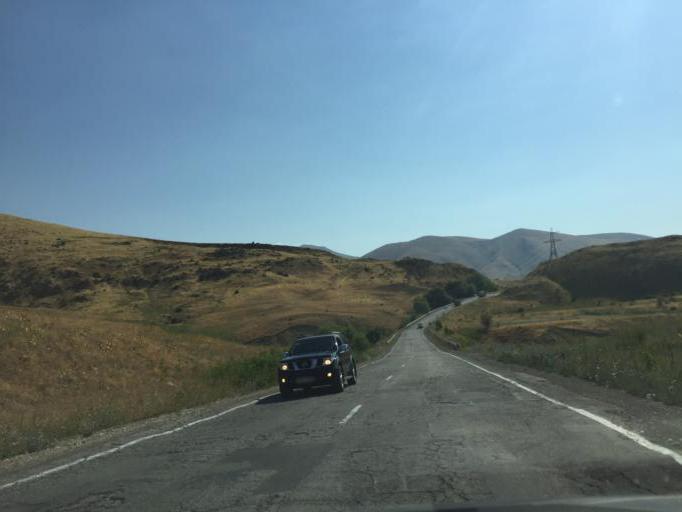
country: AM
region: Ararat
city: Zangakatun
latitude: 39.8200
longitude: 45.0115
